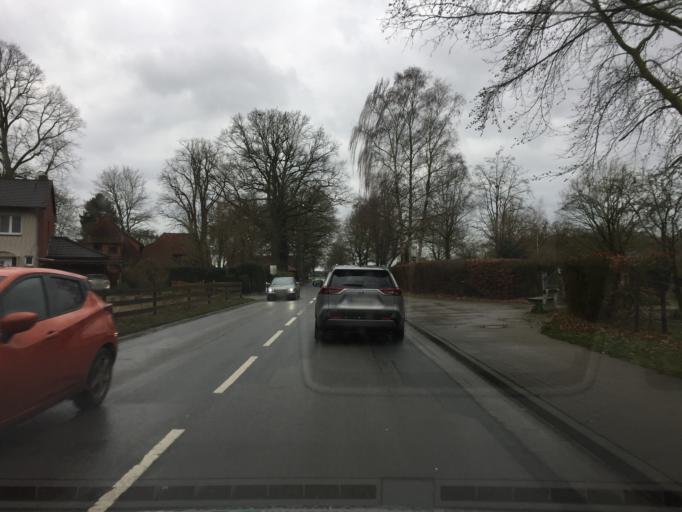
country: DE
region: Lower Saxony
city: Kirchseelte
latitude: 52.9795
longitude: 8.7091
